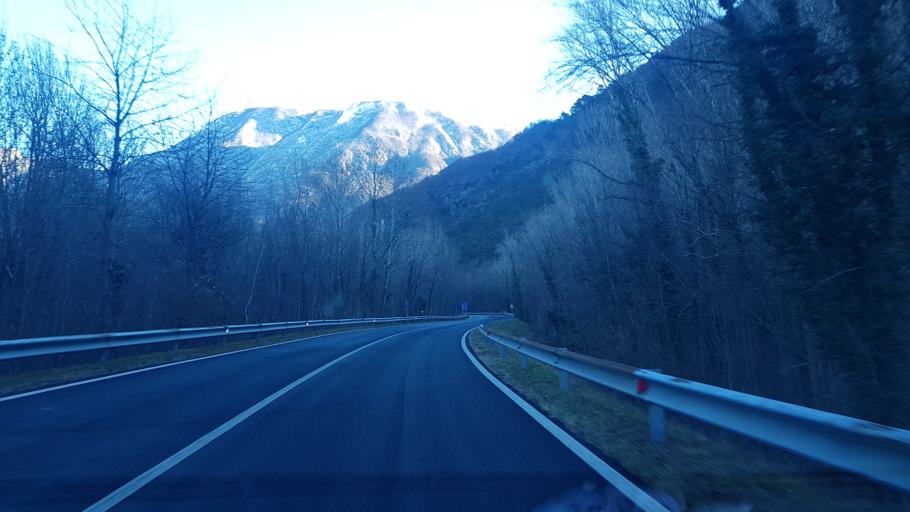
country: IT
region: Friuli Venezia Giulia
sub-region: Provincia di Udine
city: Trasaghis
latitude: 46.3153
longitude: 13.0627
